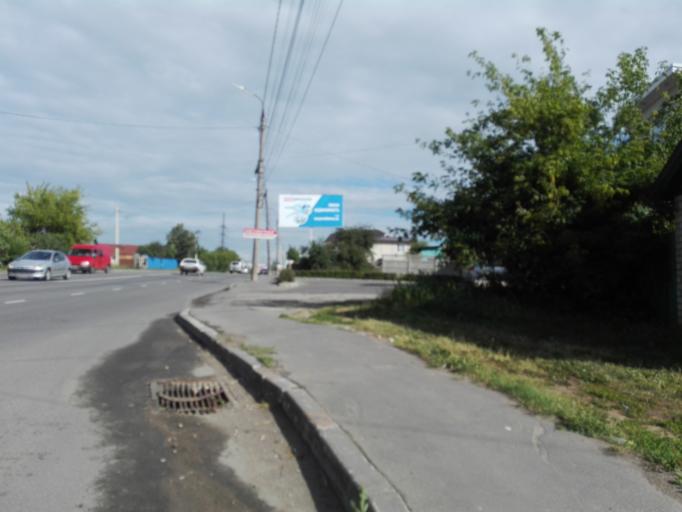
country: RU
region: Orjol
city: Orel
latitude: 52.9965
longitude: 36.1096
